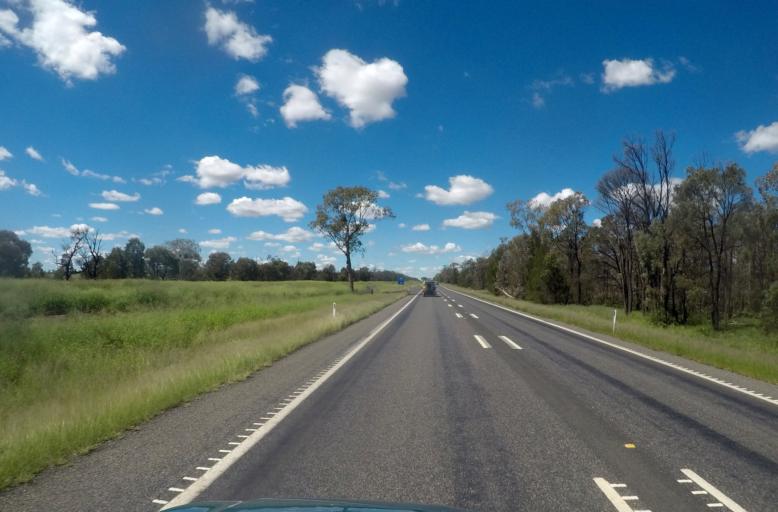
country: AU
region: Queensland
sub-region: Western Downs
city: Chinchilla
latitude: -26.6827
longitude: 150.4642
